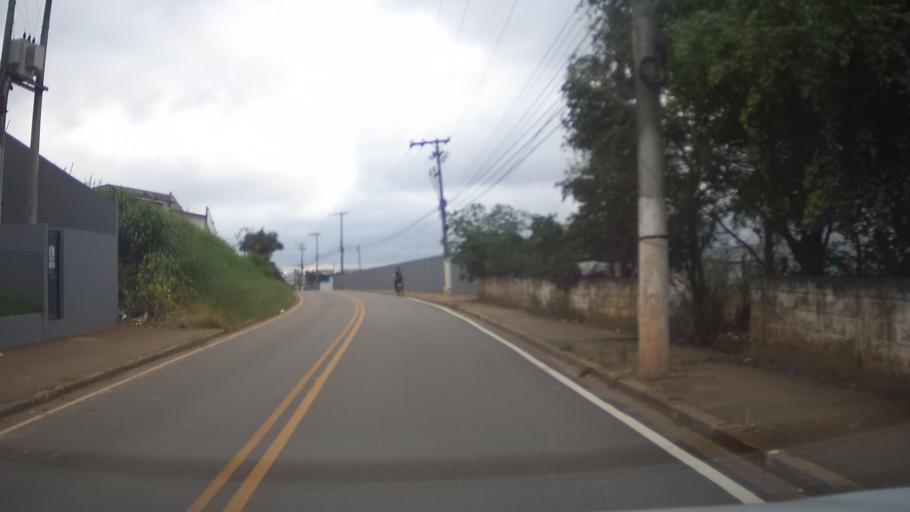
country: BR
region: Sao Paulo
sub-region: Aruja
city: Aruja
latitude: -23.4044
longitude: -46.3572
